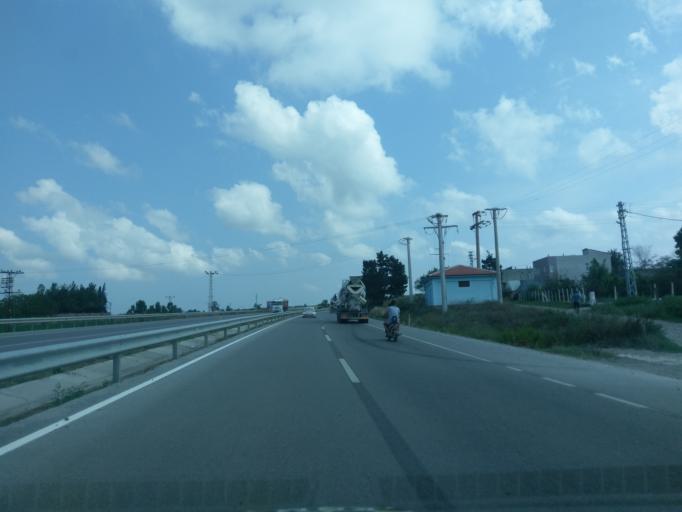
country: TR
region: Samsun
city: Bafra
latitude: 41.6041
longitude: 35.8106
